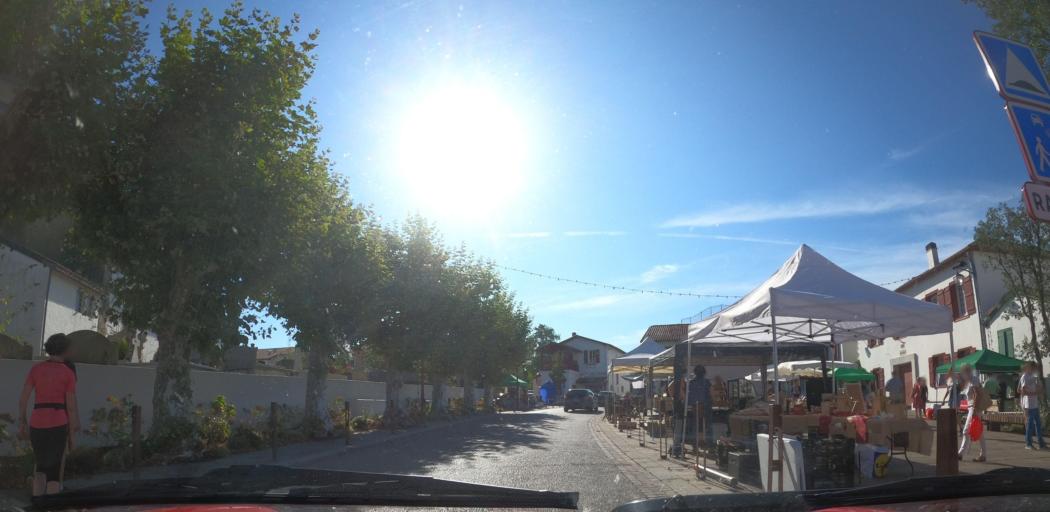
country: FR
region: Aquitaine
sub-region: Departement des Pyrenees-Atlantiques
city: Arbonne
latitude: 43.4323
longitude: -1.5519
